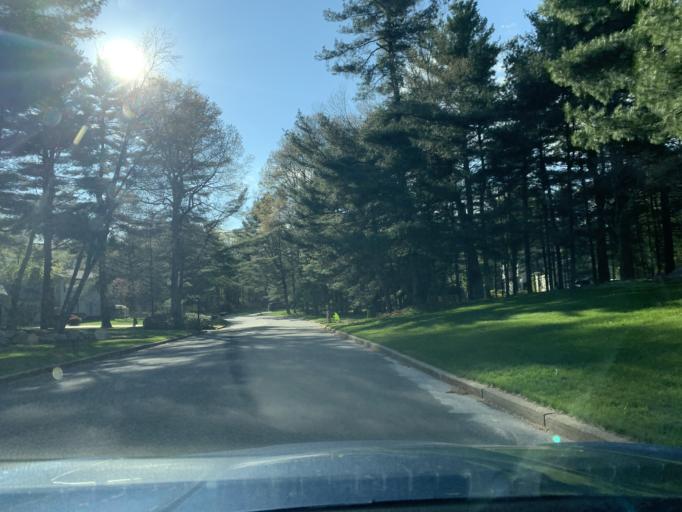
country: US
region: Rhode Island
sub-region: Washington County
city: Exeter
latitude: 41.6321
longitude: -71.5295
